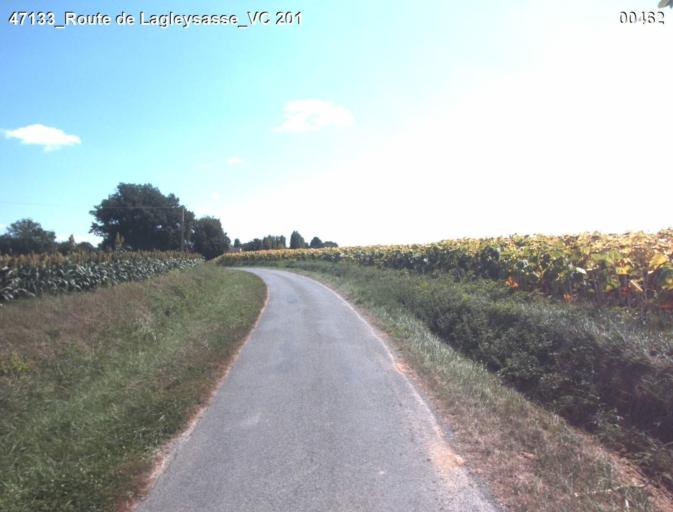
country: FR
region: Aquitaine
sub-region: Departement du Lot-et-Garonne
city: Laplume
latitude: 44.0596
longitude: 0.5541
